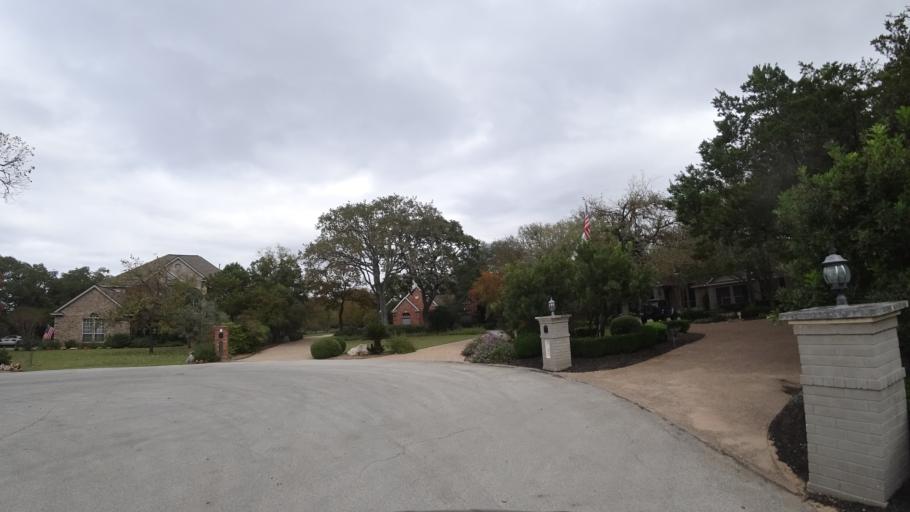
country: US
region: Texas
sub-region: Travis County
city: Shady Hollow
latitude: 30.1532
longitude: -97.8658
